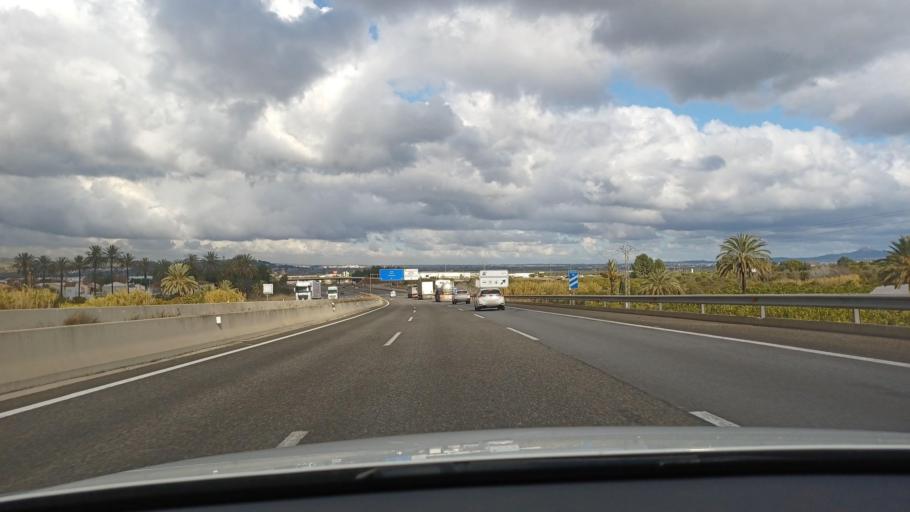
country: ES
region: Valencia
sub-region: Provincia de Valencia
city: Beneixida
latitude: 39.0528
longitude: -0.5458
